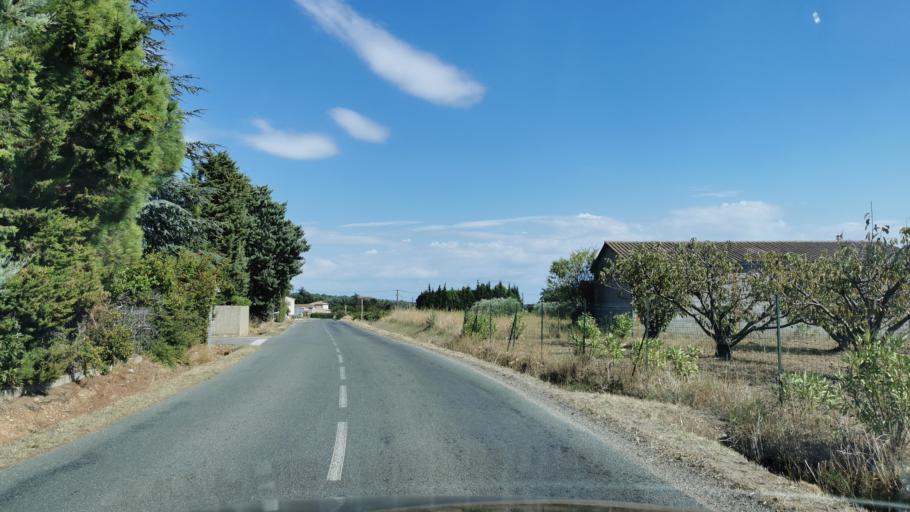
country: FR
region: Languedoc-Roussillon
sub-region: Departement de l'Aude
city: Peyriac-Minervois
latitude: 43.3105
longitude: 2.5607
